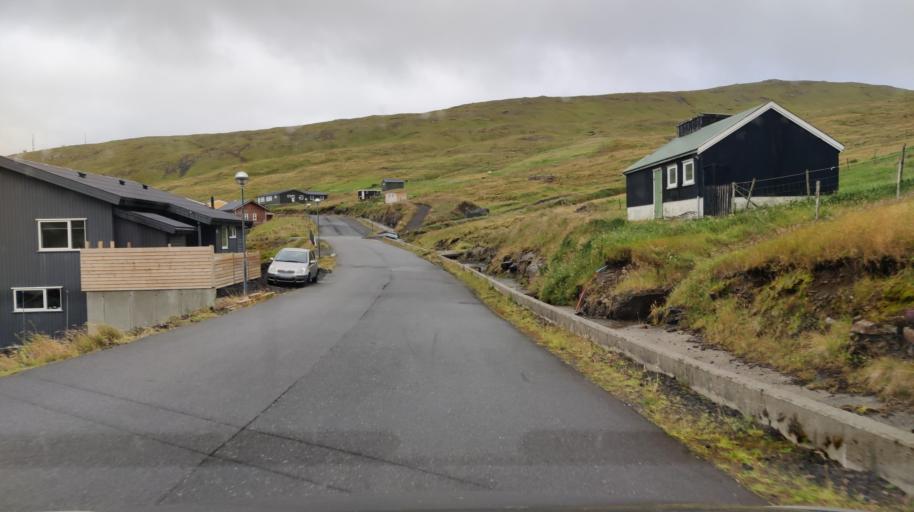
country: FO
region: Streymoy
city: Vestmanna
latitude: 62.1566
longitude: -7.1829
